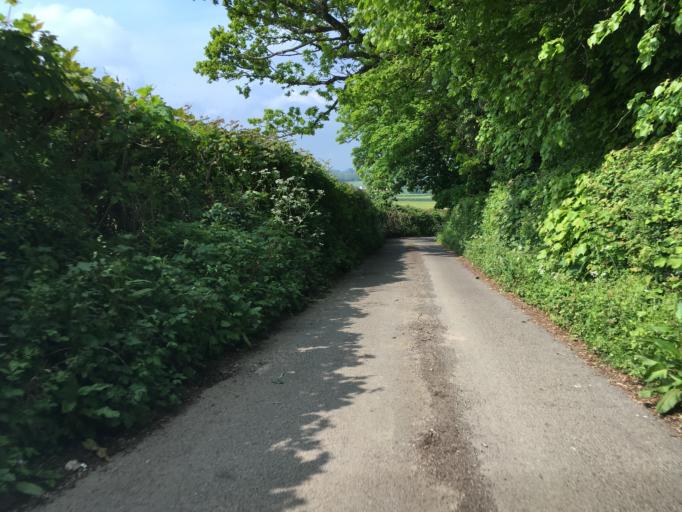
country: GB
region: England
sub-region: North Somerset
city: Winford
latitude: 51.3865
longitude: -2.6542
